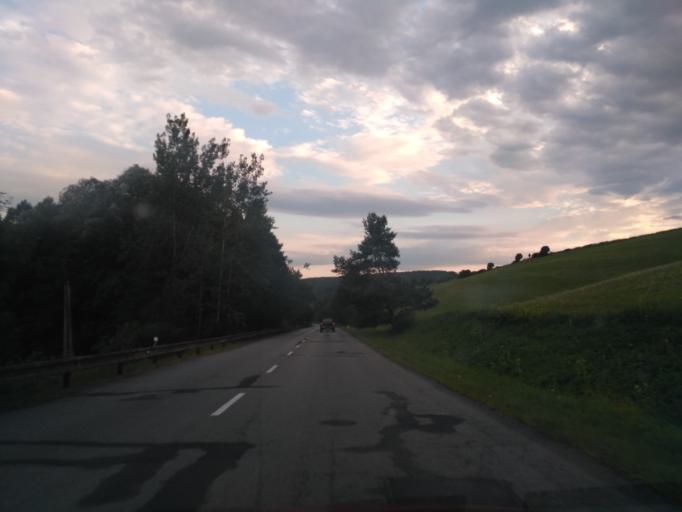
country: SK
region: Presovsky
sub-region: Okres Presov
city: Presov
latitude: 48.9628
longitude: 21.1662
